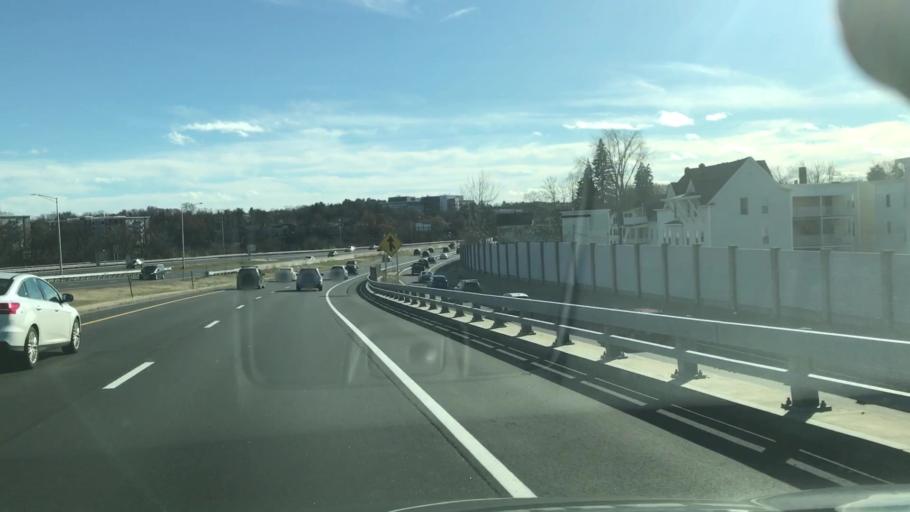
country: US
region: New Hampshire
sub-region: Hillsborough County
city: Manchester
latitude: 42.9838
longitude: -71.4708
